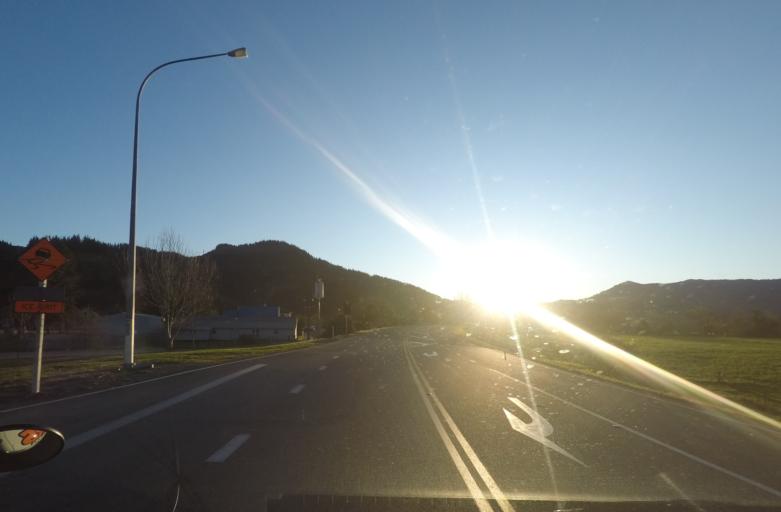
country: NZ
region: Marlborough
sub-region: Marlborough District
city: Picton
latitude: -41.2912
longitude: 173.6718
